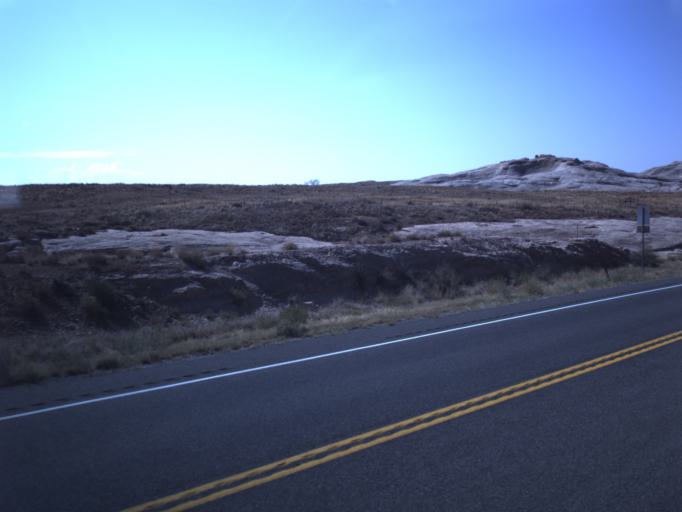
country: US
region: Utah
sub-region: San Juan County
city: Blanding
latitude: 37.2993
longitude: -109.5340
